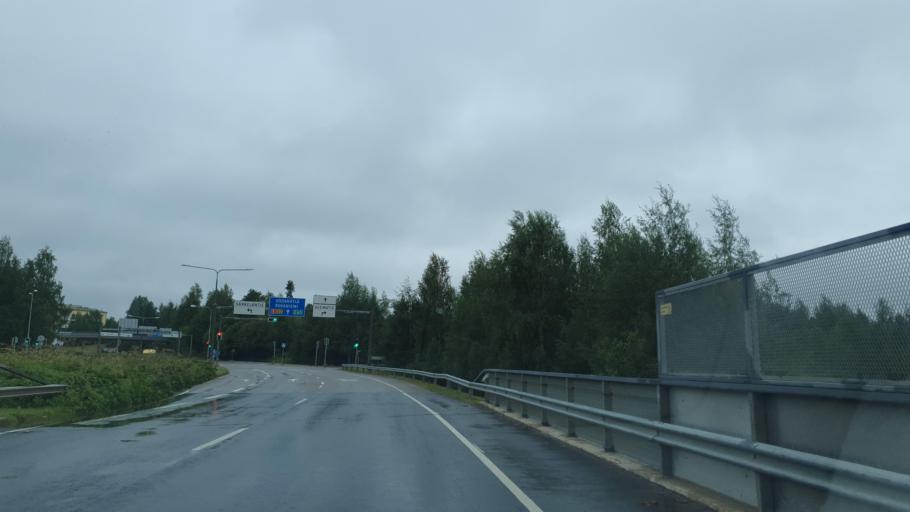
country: FI
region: Lapland
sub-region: Itae-Lappi
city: Kemijaervi
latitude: 66.7209
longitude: 27.4039
